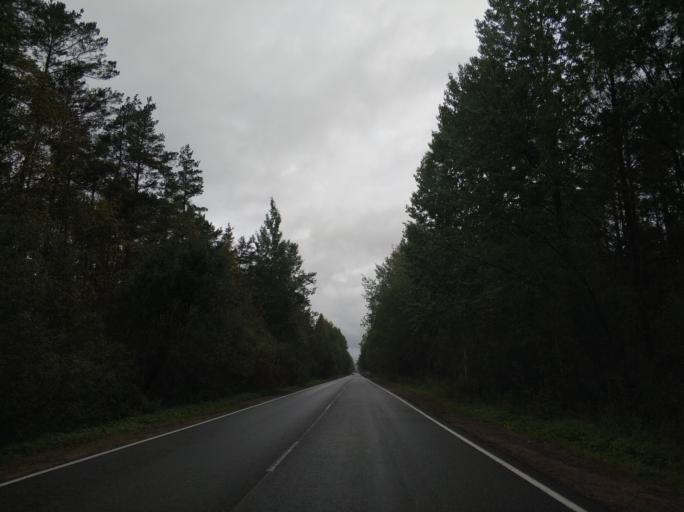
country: RU
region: Leningrad
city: Borisova Griva
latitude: 60.1502
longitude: 30.9380
